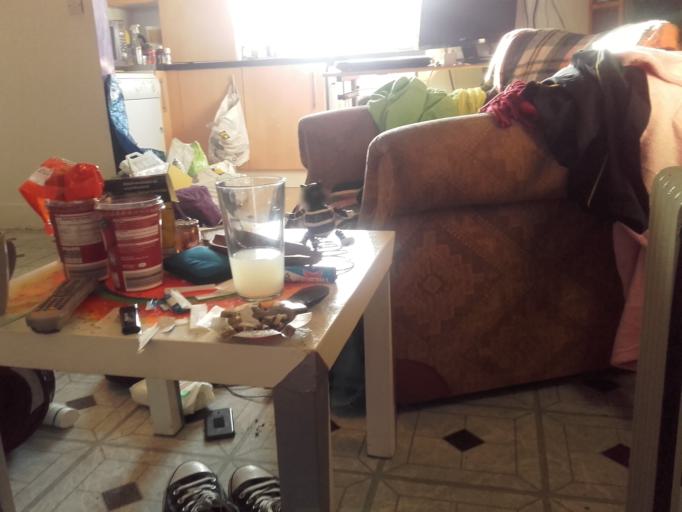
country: GB
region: England
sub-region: Kent
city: Hawkinge
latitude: 51.1100
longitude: 1.1525
